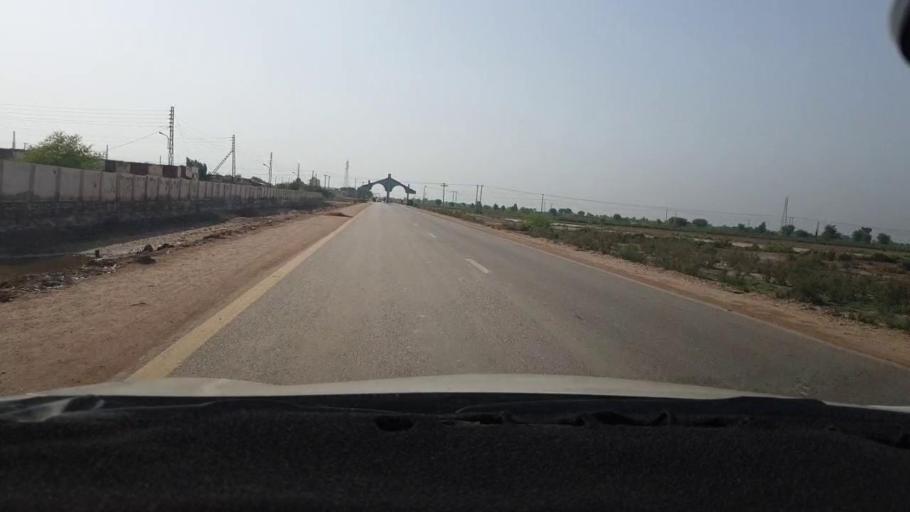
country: PK
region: Sindh
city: Sanghar
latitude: 26.0305
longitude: 68.9531
